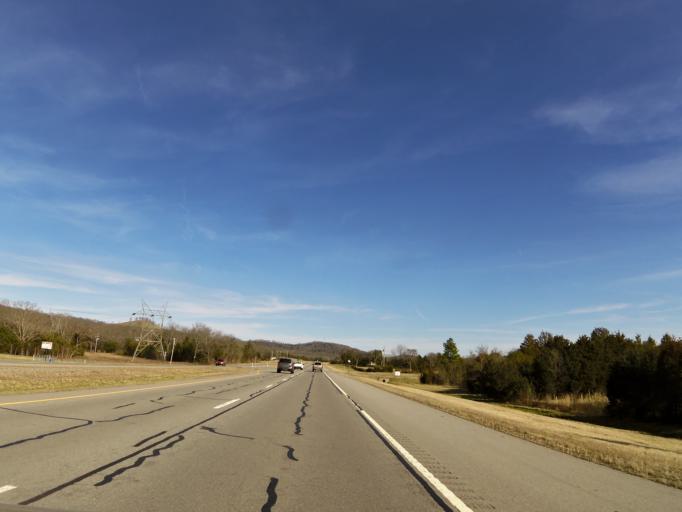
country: US
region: Tennessee
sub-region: Rutherford County
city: Murfreesboro
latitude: 35.8190
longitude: -86.2389
